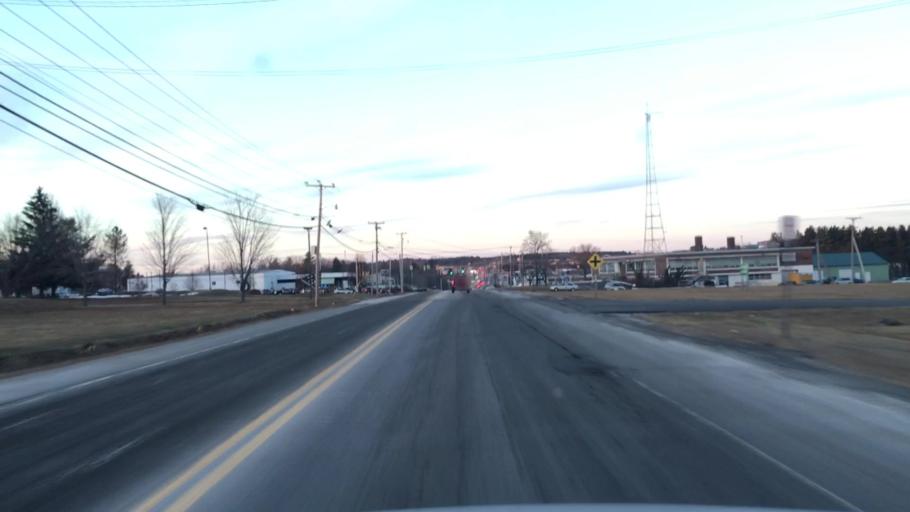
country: US
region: Maine
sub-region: Penobscot County
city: Brewer
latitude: 44.8204
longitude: -68.7391
